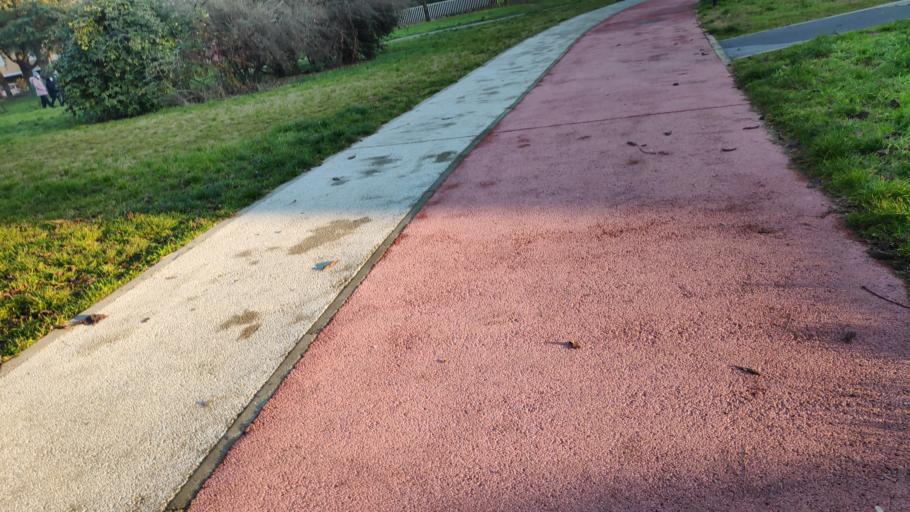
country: IT
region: Lombardy
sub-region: Citta metropolitana di Milano
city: Cologno Monzese
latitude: 45.5293
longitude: 9.2826
